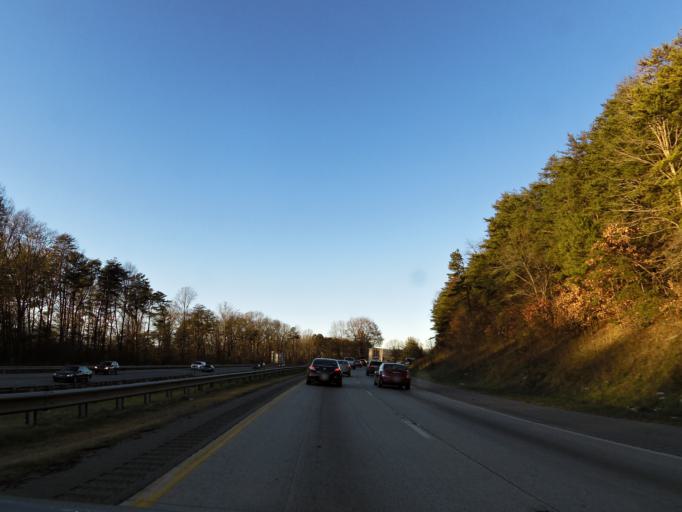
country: US
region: North Carolina
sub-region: Buncombe County
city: Royal Pines
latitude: 35.4508
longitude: -82.5417
